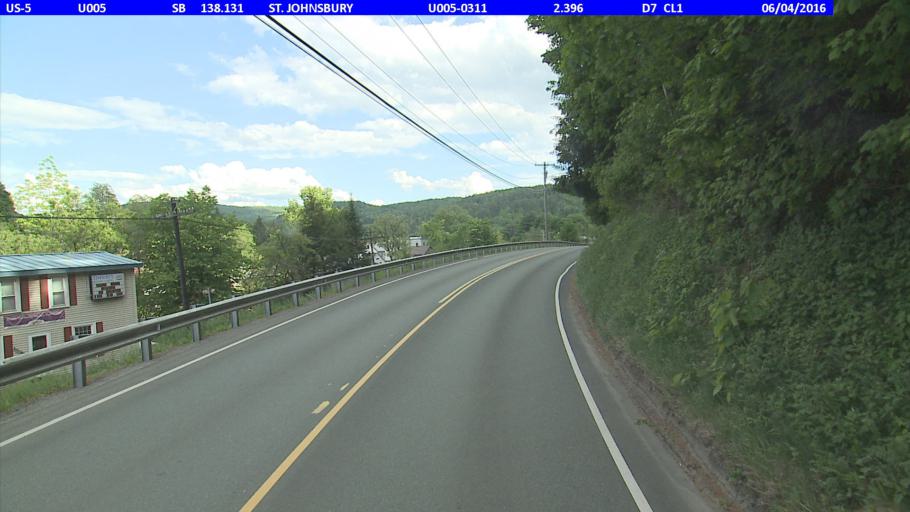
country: US
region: Vermont
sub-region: Caledonia County
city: St Johnsbury
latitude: 44.4275
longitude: -72.0157
